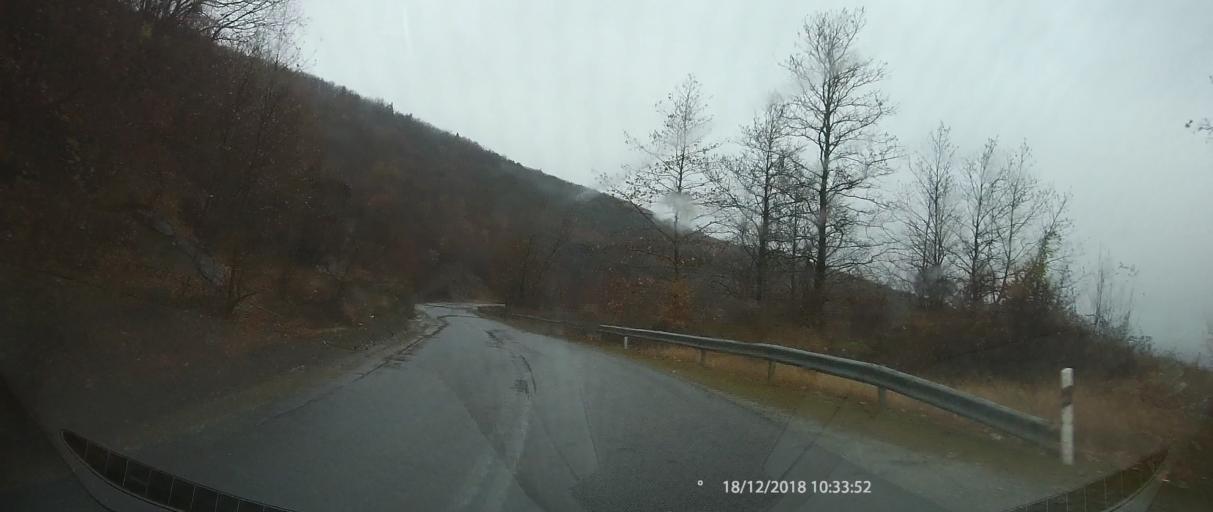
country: GR
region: Central Macedonia
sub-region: Nomos Pierias
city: Kato Milia
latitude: 40.2015
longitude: 22.3010
